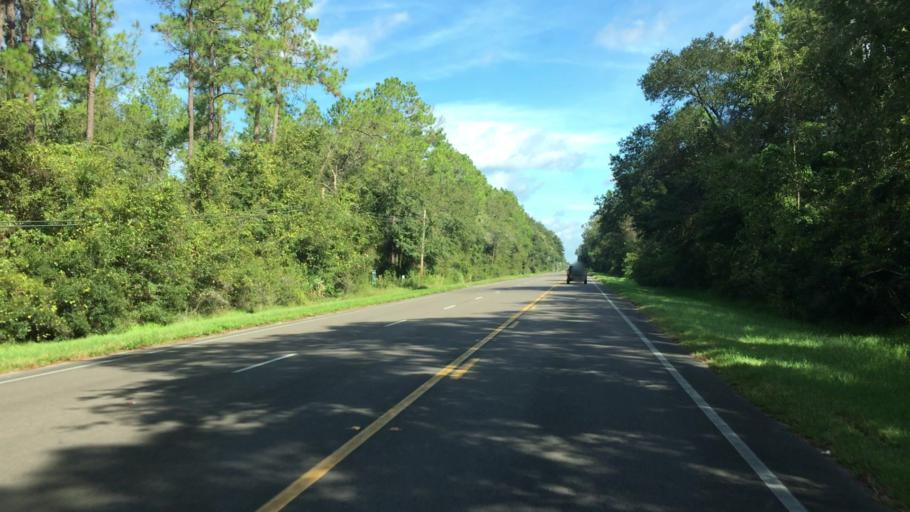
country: US
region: Florida
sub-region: Alachua County
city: Gainesville
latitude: 29.7128
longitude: -82.2773
